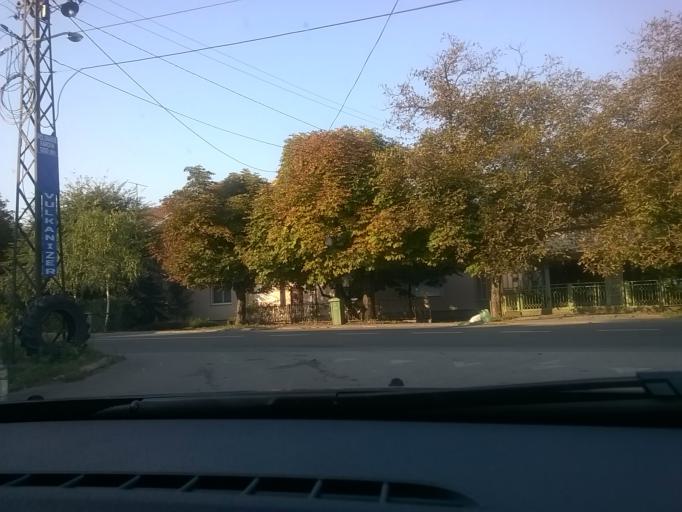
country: RS
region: Autonomna Pokrajina Vojvodina
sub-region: Juznobanatski Okrug
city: Vrsac
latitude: 45.1189
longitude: 21.2846
